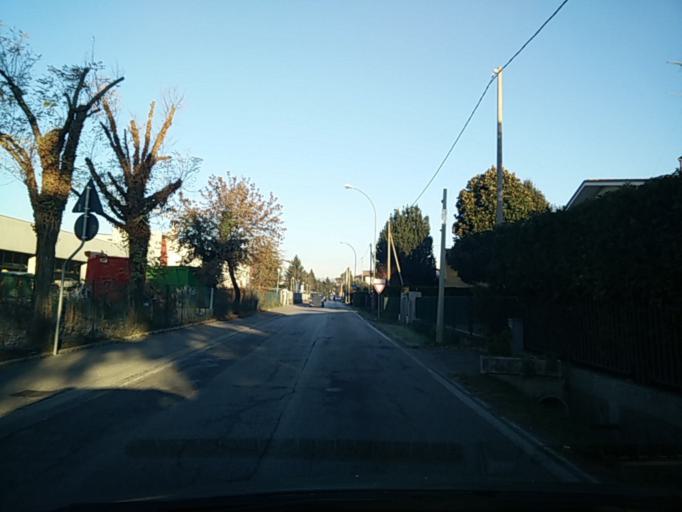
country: IT
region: Veneto
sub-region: Provincia di Treviso
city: Lancenigo-Villorba
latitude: 45.6921
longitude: 12.2534
